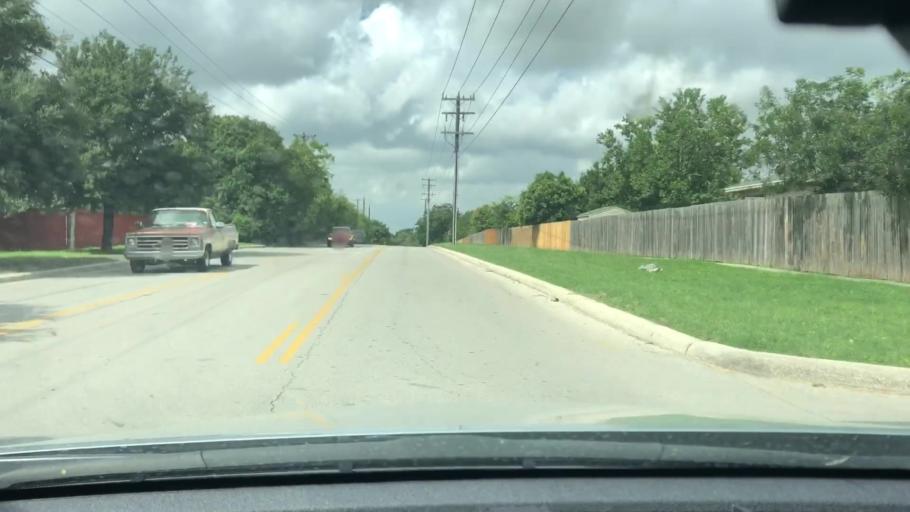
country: US
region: Texas
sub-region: Bexar County
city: Windcrest
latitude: 29.5315
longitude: -98.3746
